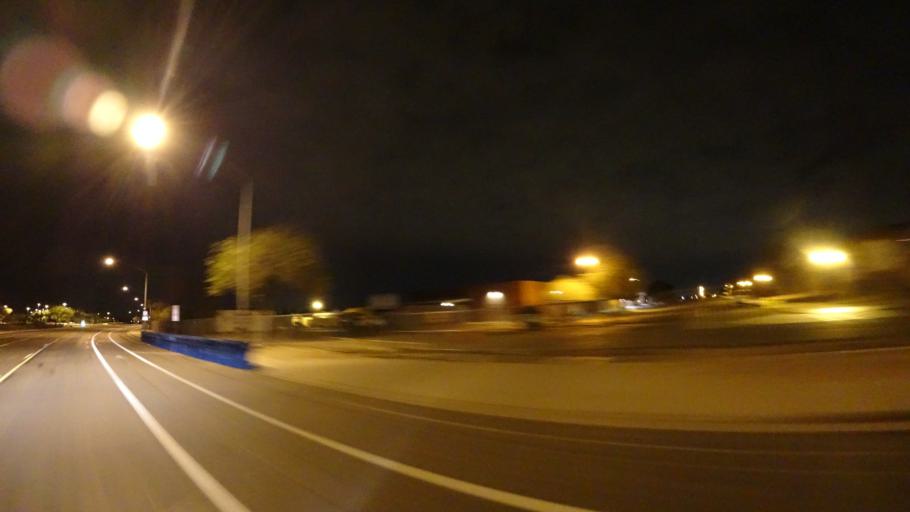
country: US
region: Arizona
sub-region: Pinal County
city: Apache Junction
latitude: 33.4340
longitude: -111.6719
